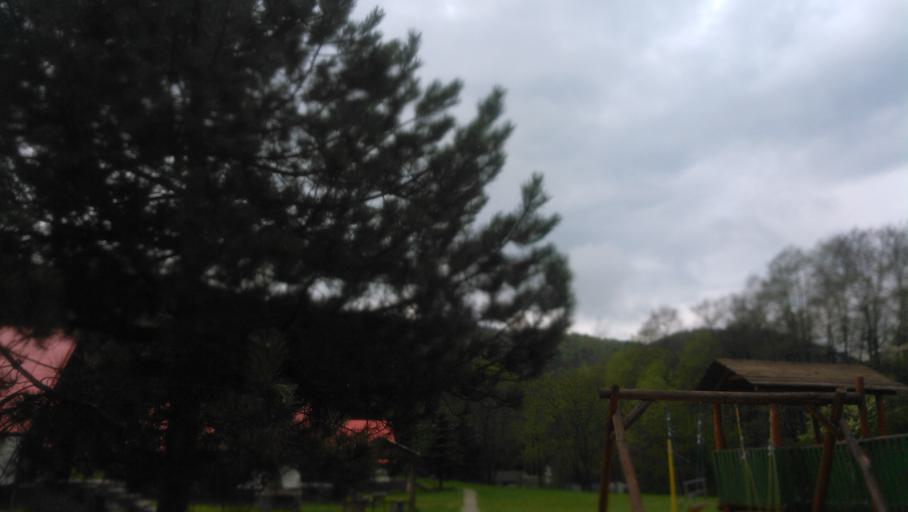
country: SK
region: Banskobystricky
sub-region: Okres Banska Bystrica
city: Brezno
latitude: 48.8481
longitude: 19.6070
